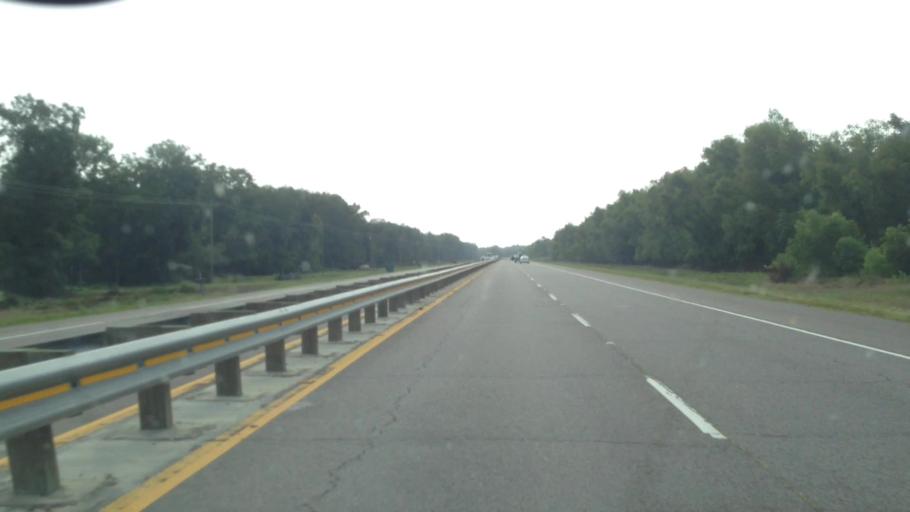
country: US
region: Louisiana
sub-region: Iberville Parish
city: Maringouin
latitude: 30.5528
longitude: -91.4792
